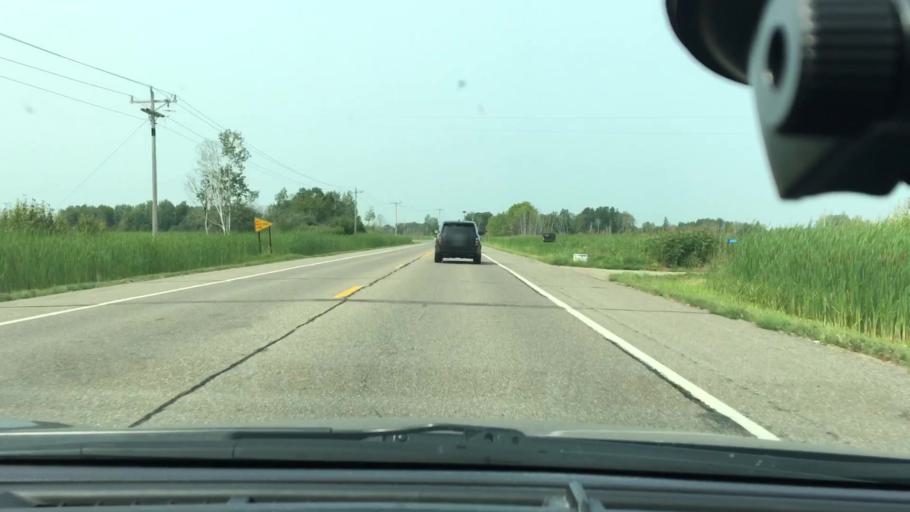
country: US
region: Minnesota
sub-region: Crow Wing County
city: Brainerd
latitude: 46.3985
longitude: -94.2176
